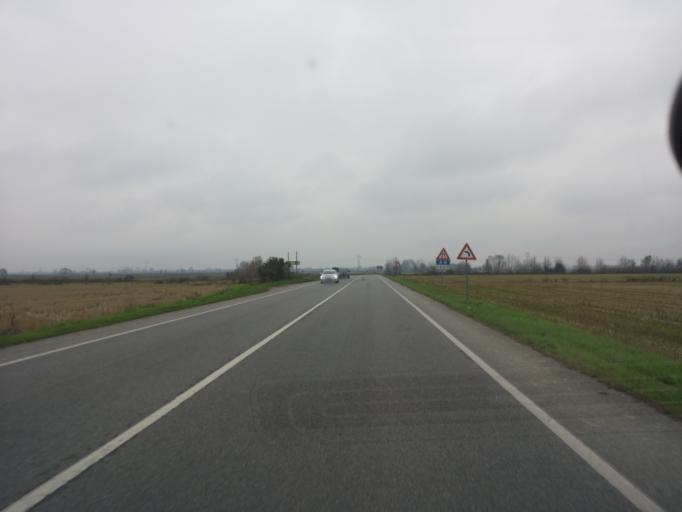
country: IT
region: Piedmont
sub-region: Provincia di Vercelli
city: Stroppiana
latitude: 45.2042
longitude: 8.4618
